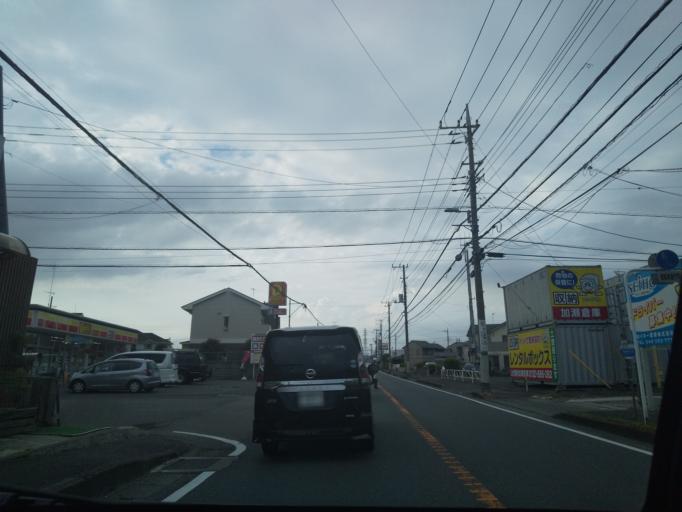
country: JP
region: Kanagawa
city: Zama
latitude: 35.4751
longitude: 139.3890
